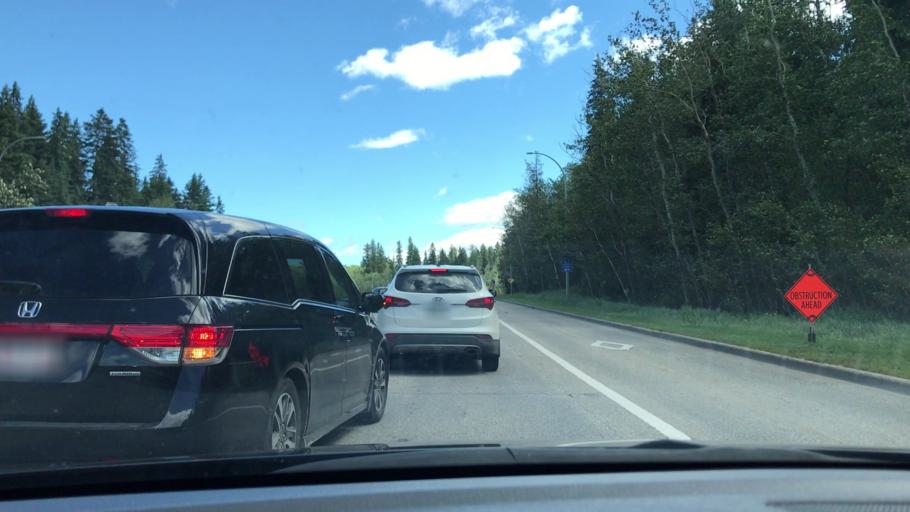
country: CA
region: Alberta
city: Edmonton
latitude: 53.5053
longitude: -113.5427
